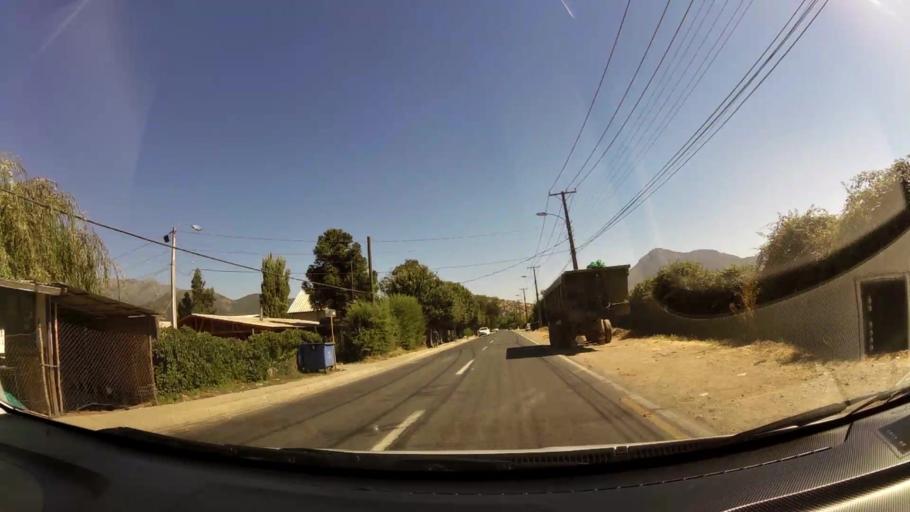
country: CL
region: O'Higgins
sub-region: Provincia de Cachapoal
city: Graneros
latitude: -33.9663
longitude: -70.7130
